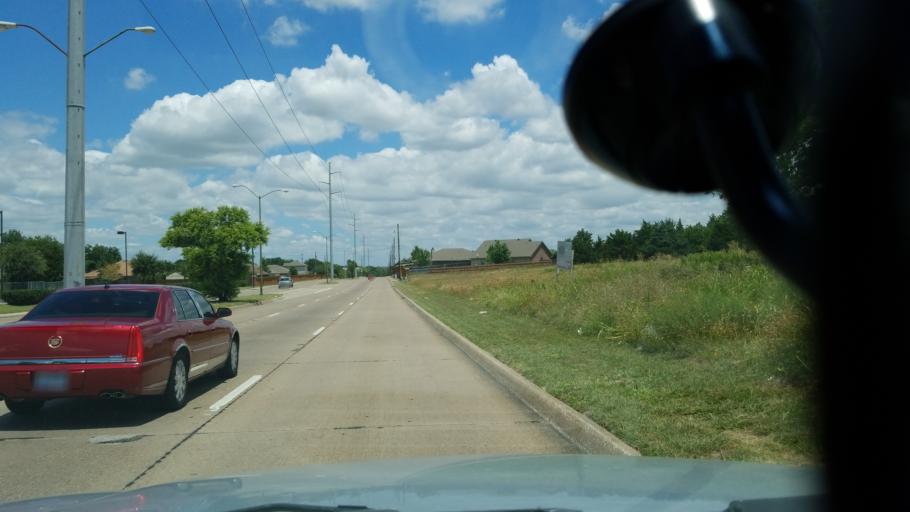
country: US
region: Texas
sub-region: Dallas County
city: Duncanville
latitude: 32.6642
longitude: -96.8816
